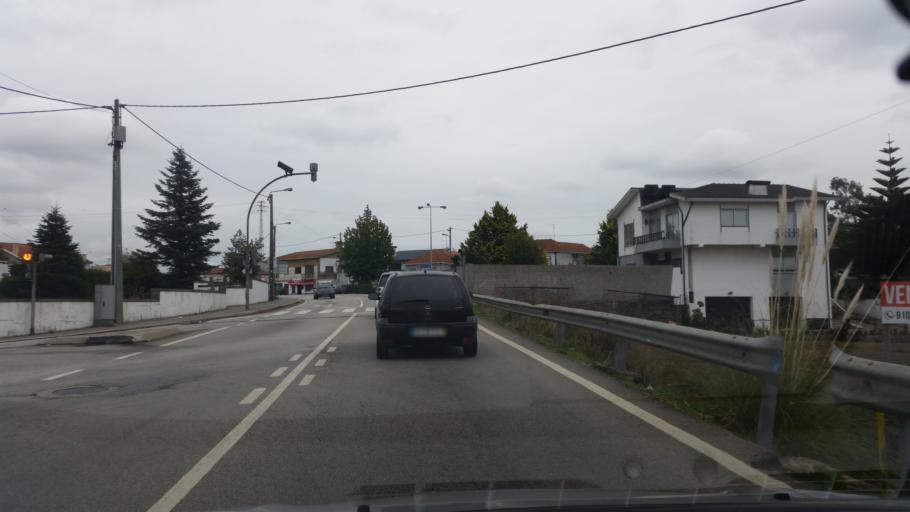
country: PT
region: Porto
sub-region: Valongo
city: Ermesinde
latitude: 41.2326
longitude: -8.5456
